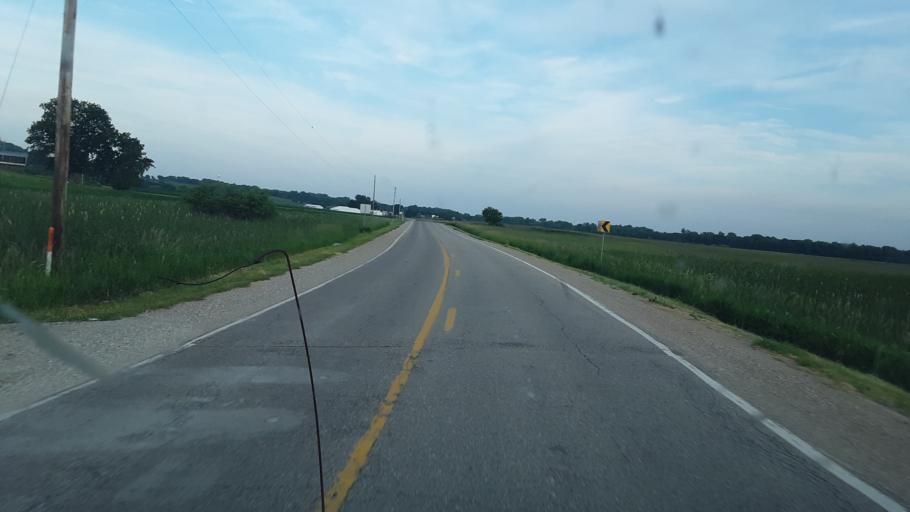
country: US
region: Iowa
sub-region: Benton County
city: Belle Plaine
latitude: 41.9415
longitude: -92.4140
